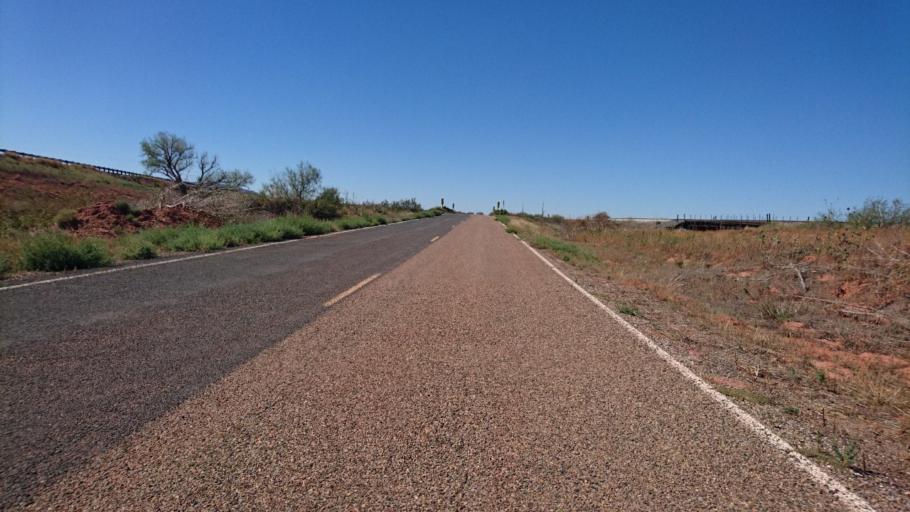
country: US
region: New Mexico
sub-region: Quay County
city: Tucumcari
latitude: 35.0999
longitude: -104.0510
